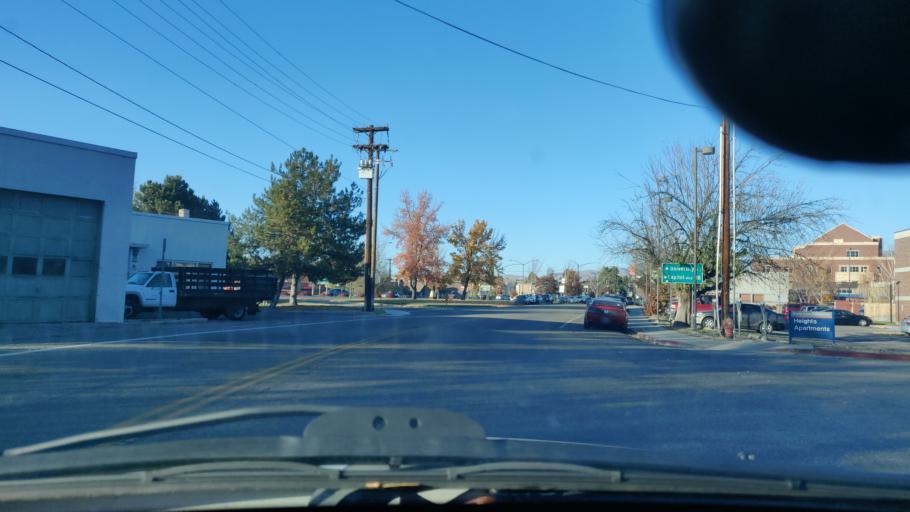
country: US
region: Idaho
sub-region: Ada County
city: Boise
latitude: 43.6036
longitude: -116.2118
